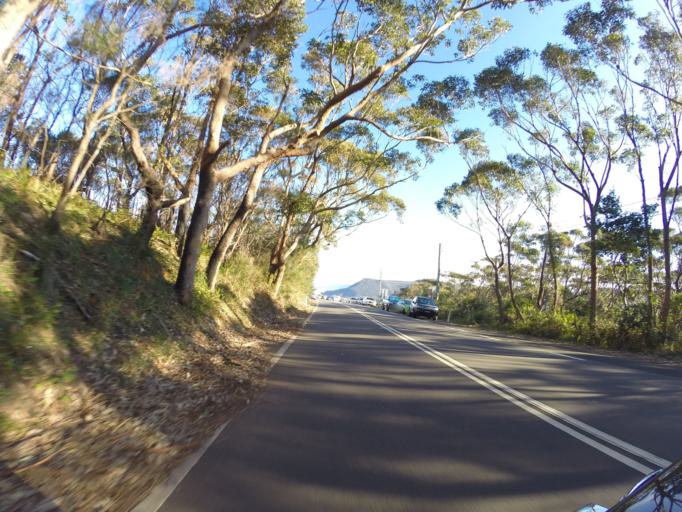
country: AU
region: New South Wales
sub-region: Wollongong
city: Helensburgh
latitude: -34.2225
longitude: 150.9984
